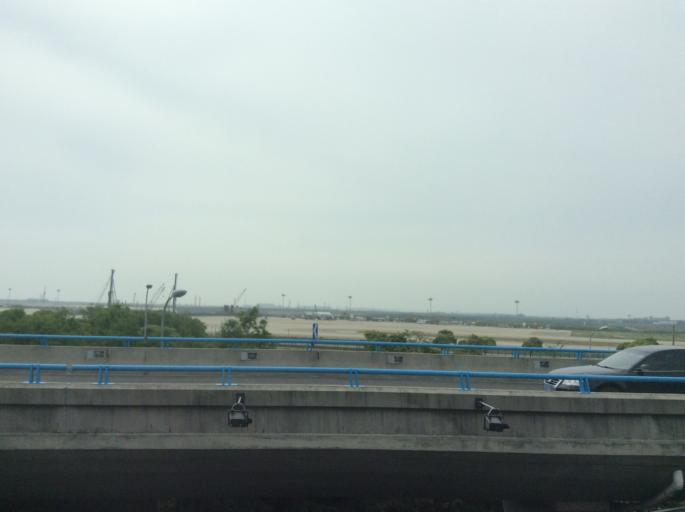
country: CN
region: Shanghai Shi
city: Laogang
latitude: 31.1457
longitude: 121.8052
